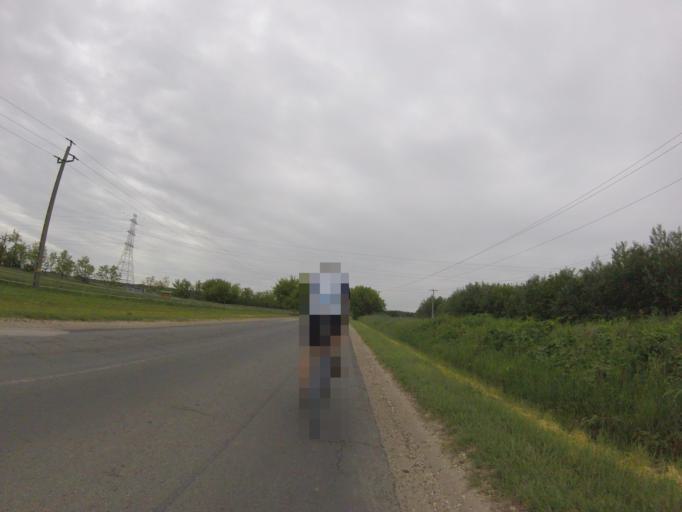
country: HU
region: Pest
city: Bugyi
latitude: 47.2328
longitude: 19.1826
